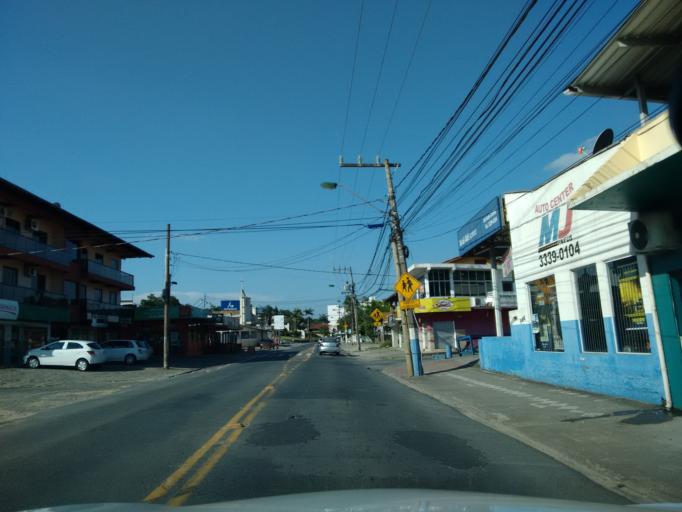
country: BR
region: Santa Catarina
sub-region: Blumenau
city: Blumenau
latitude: -26.8788
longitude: -49.0674
